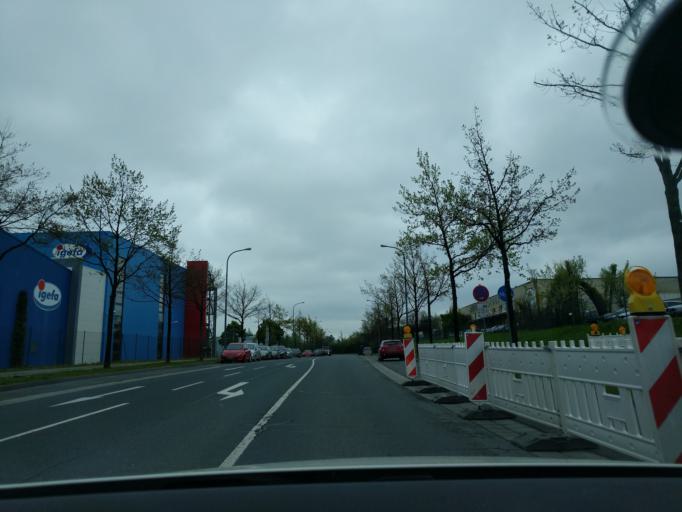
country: DE
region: Saxony
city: Bannewitz
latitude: 51.0080
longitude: 13.6945
